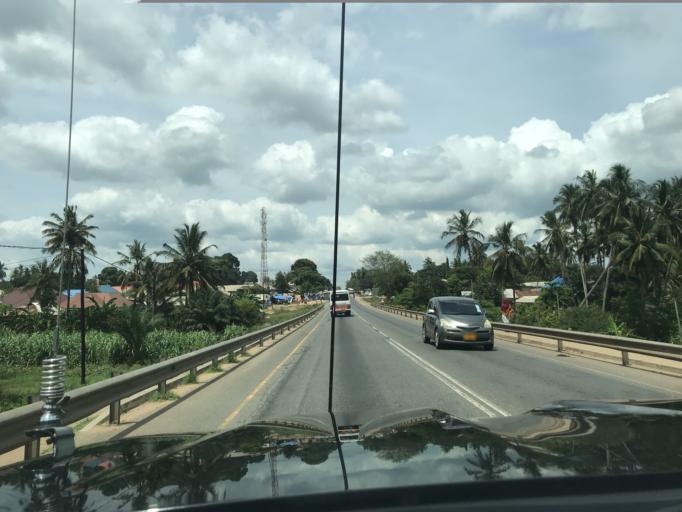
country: TZ
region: Pwani
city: Kibaha
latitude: -6.7393
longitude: 38.8725
